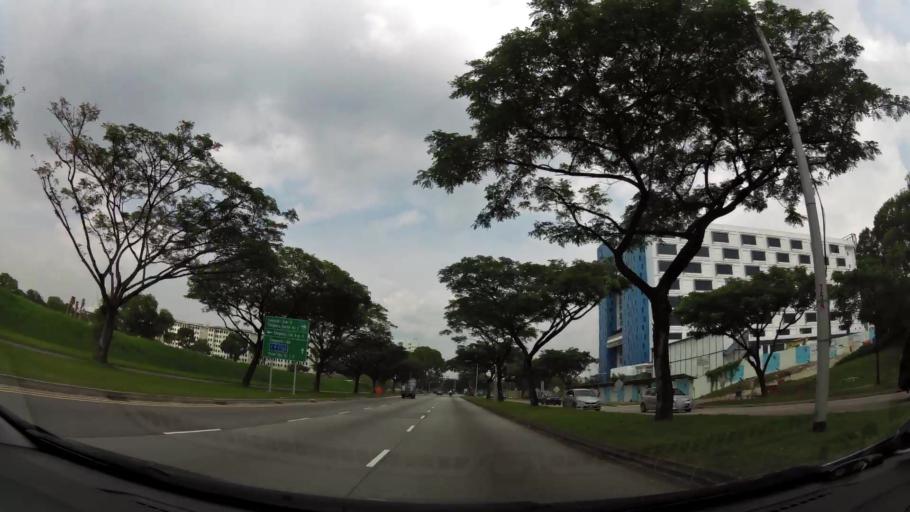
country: SG
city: Singapore
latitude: 1.3645
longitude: 103.9309
